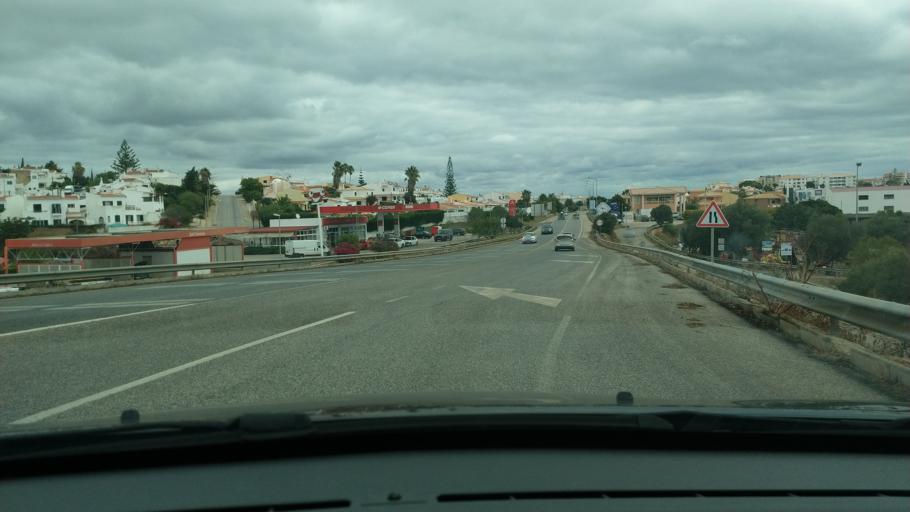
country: PT
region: Faro
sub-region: Lagos
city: Lagos
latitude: 37.1016
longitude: -8.6940
